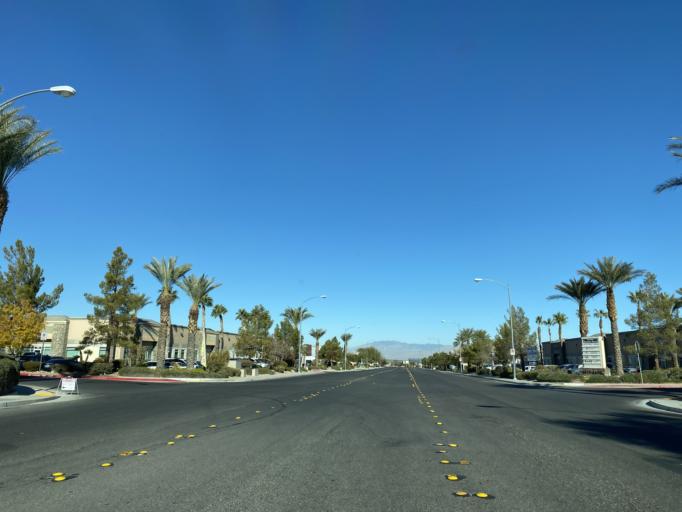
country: US
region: Nevada
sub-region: Clark County
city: Spring Valley
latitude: 36.0672
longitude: -115.2516
